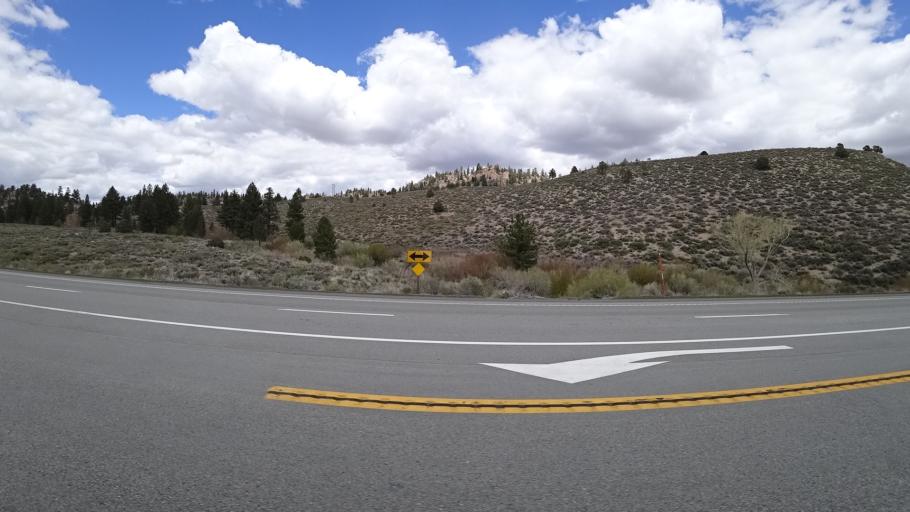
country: US
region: California
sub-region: Inyo County
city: West Bishop
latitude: 37.5581
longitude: -118.6604
